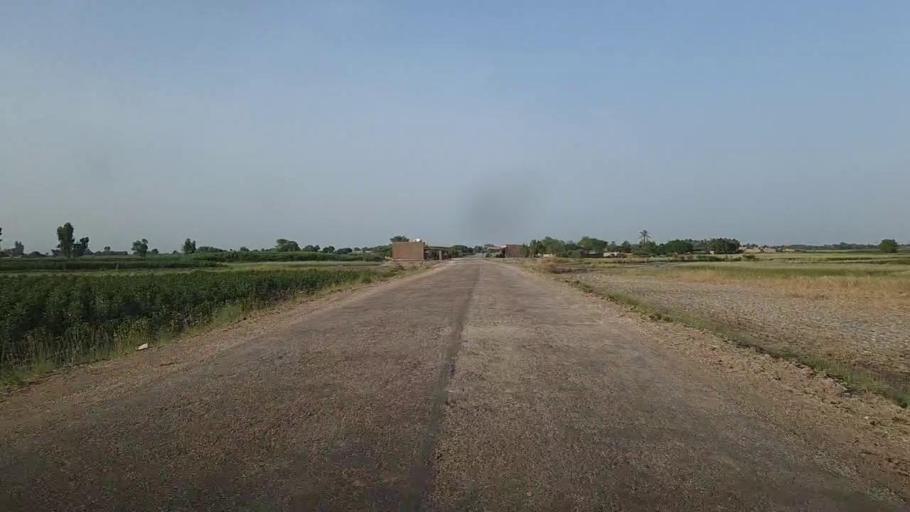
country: PK
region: Sindh
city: Ubauro
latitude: 28.1036
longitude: 69.8134
